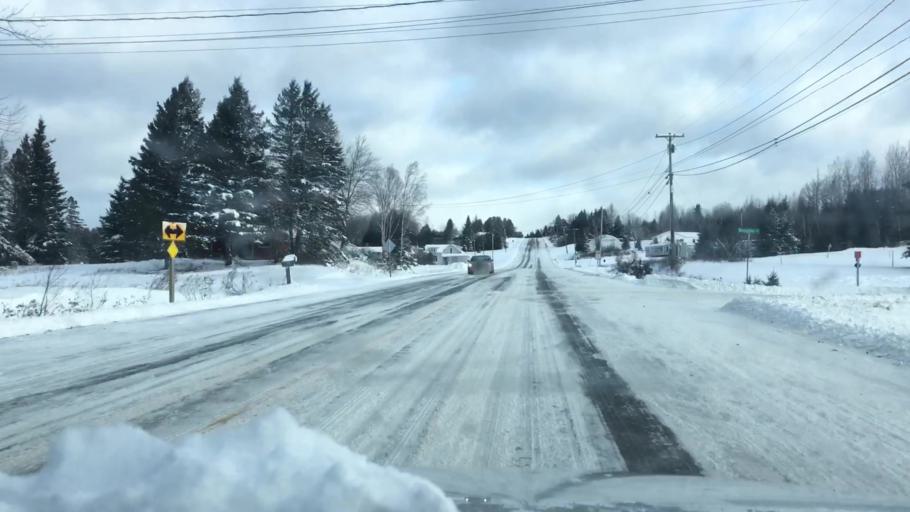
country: US
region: Maine
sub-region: Aroostook County
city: Caribou
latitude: 46.9796
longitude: -68.0347
